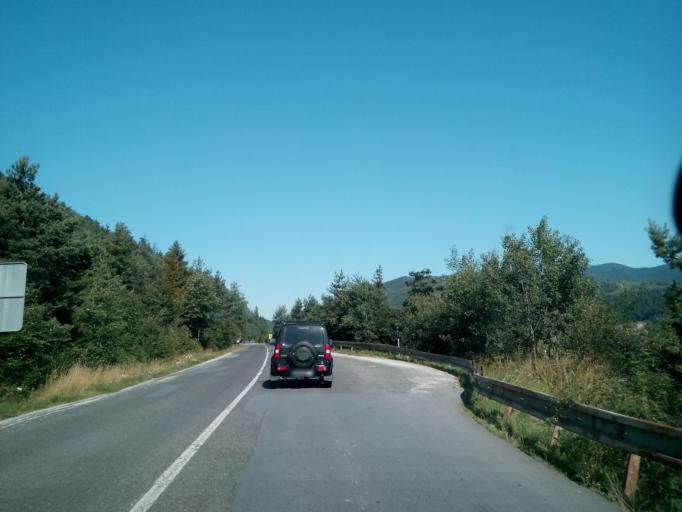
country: SK
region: Kosicky
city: Krompachy
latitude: 48.9222
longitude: 20.9218
